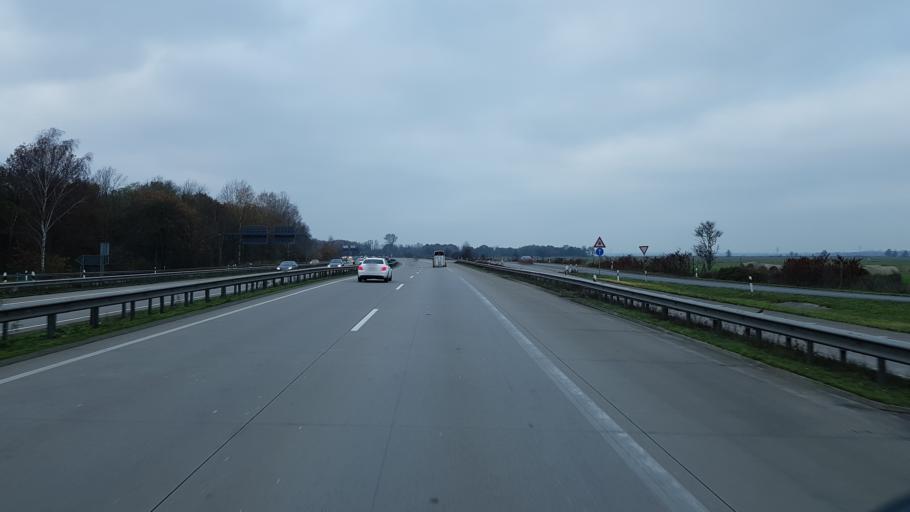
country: DE
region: Lower Saxony
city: Lilienthal
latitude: 53.1115
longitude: 8.8644
